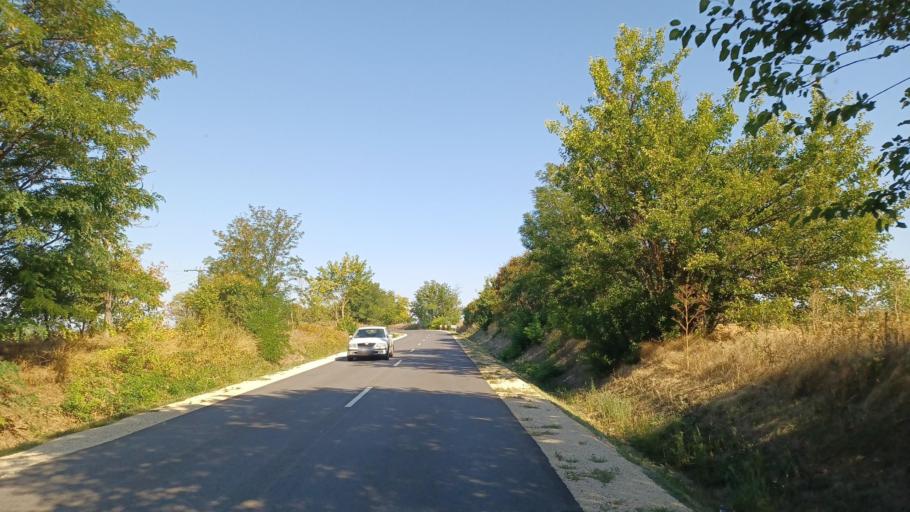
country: HU
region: Tolna
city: Paks
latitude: 46.6462
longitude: 18.8453
